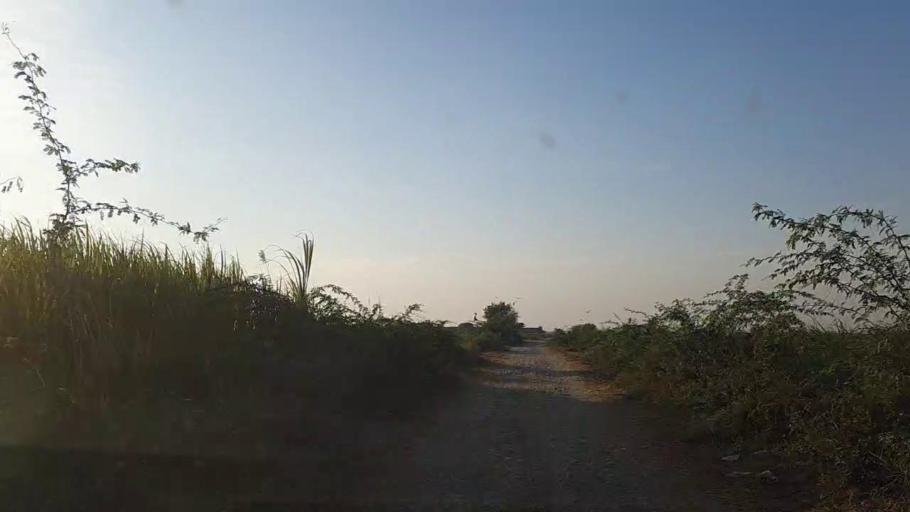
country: PK
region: Sindh
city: Mirpur Batoro
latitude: 24.6834
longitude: 68.2109
